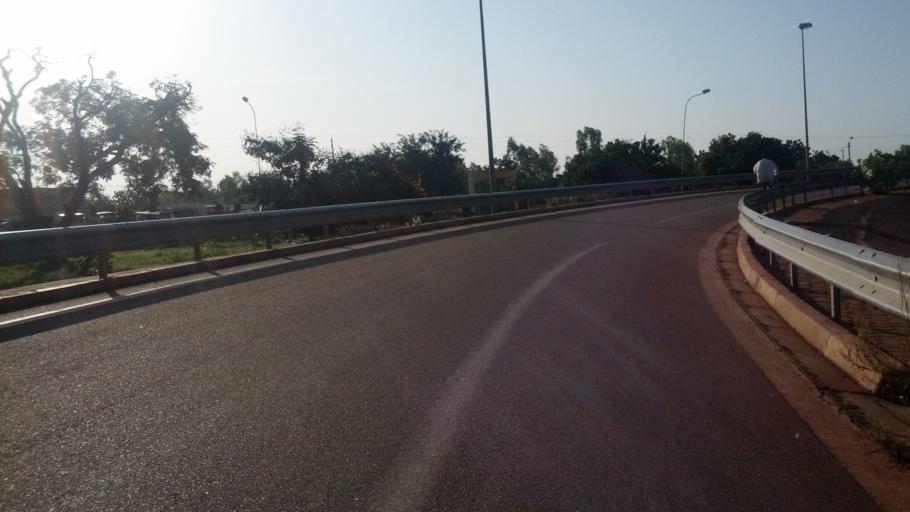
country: BF
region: Centre
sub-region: Kadiogo Province
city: Ouagadougou
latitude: 12.3330
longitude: -1.5016
